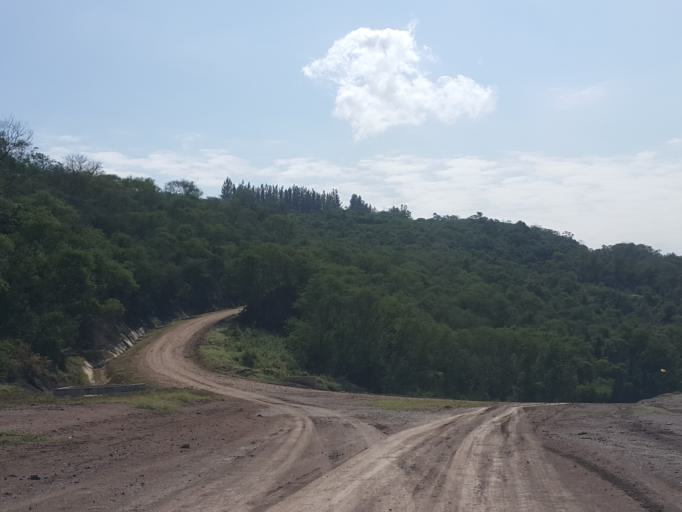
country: TH
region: Lampang
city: Mae Mo
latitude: 18.3313
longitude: 99.7389
